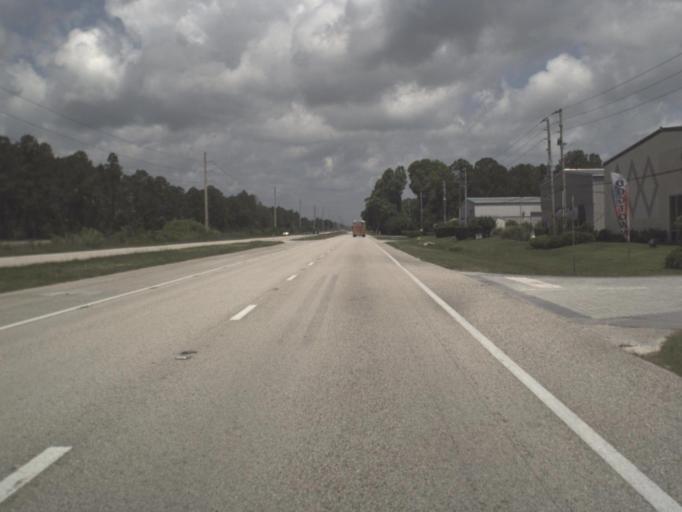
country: US
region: Florida
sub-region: Saint Johns County
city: Villano Beach
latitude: 30.0007
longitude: -81.3813
